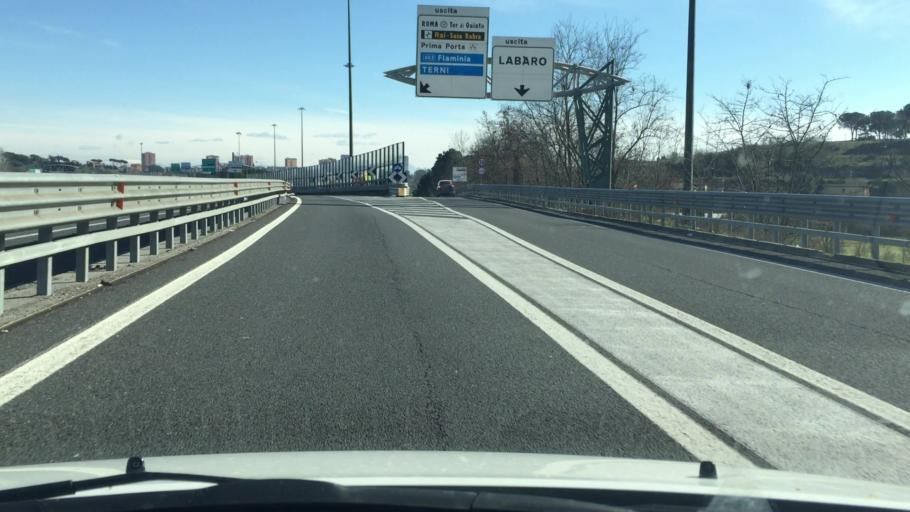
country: IT
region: Latium
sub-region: Citta metropolitana di Roma Capitale
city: Monte Caminetto
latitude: 41.9857
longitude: 12.4874
